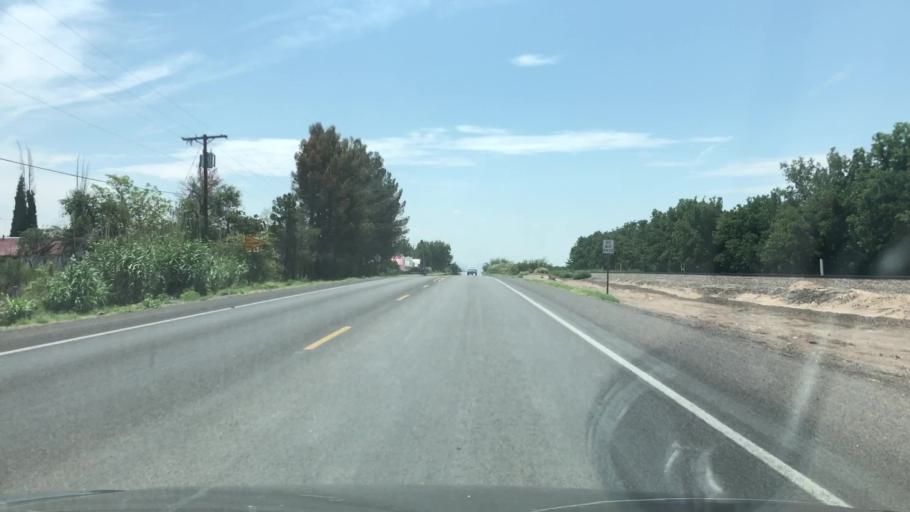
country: US
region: New Mexico
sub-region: Dona Ana County
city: Mesquite
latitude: 32.2032
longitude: -106.7210
